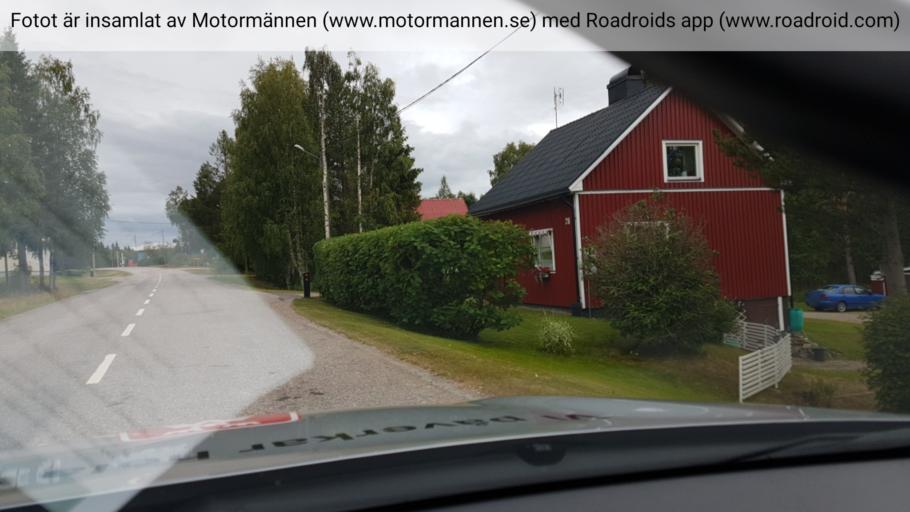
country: SE
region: Norrbotten
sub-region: Overkalix Kommun
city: OEverkalix
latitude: 66.7893
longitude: 22.9179
